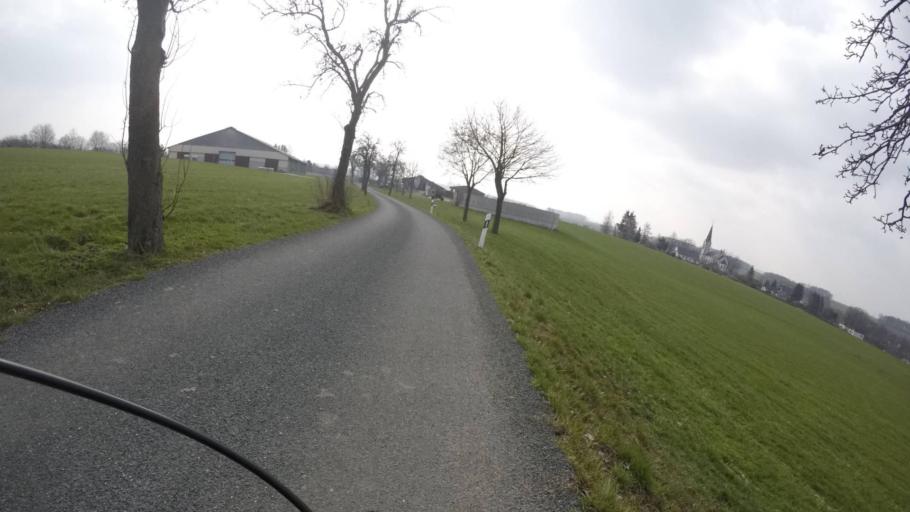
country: DE
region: Saxony
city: Niederfrohna
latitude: 50.8746
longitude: 12.6951
